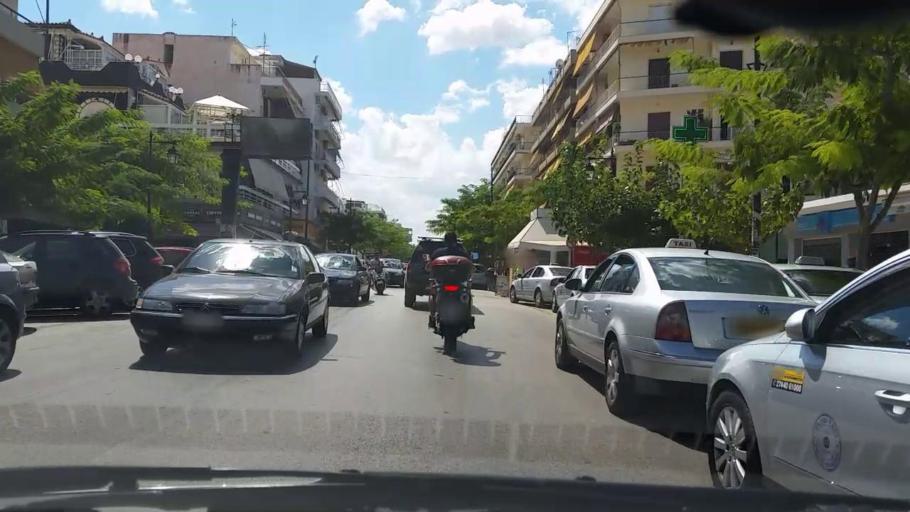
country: GR
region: Peloponnese
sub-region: Nomos Korinthias
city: Loutraki
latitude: 37.9737
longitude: 22.9777
